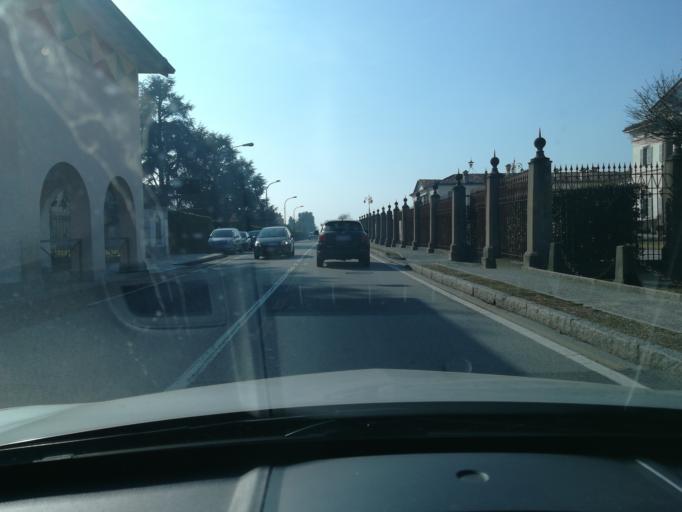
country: IT
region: Lombardy
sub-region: Provincia di Bergamo
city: Stezzano
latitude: 45.6483
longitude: 9.6518
